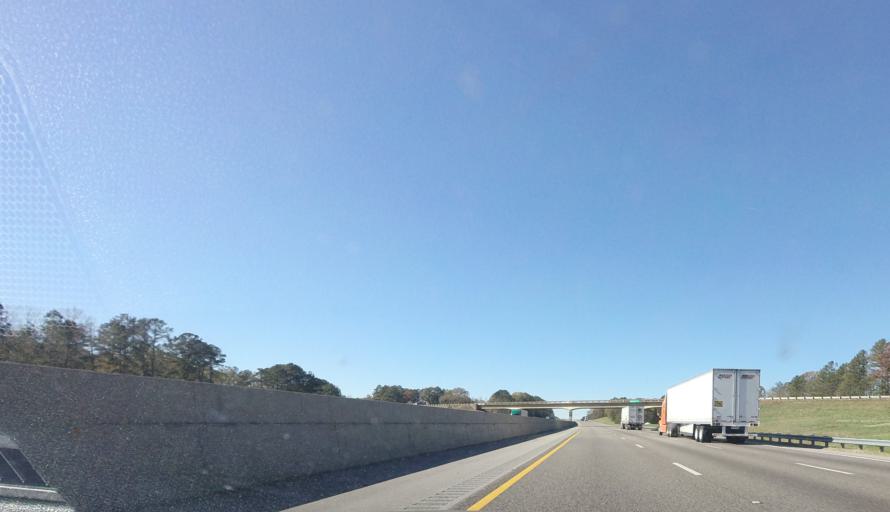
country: US
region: Alabama
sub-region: Calhoun County
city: Bynum
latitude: 33.5842
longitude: -85.9239
